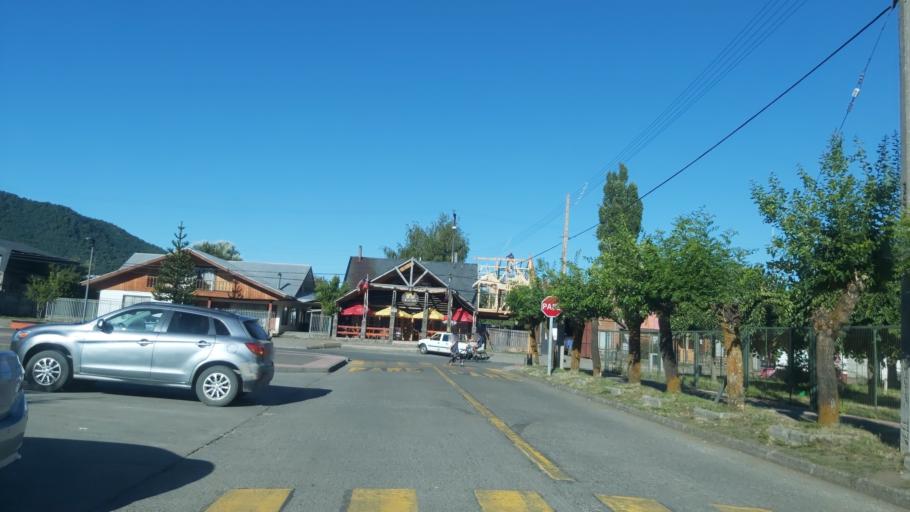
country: AR
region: Neuquen
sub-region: Departamento de Loncopue
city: Loncopue
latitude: -38.4546
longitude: -71.3701
